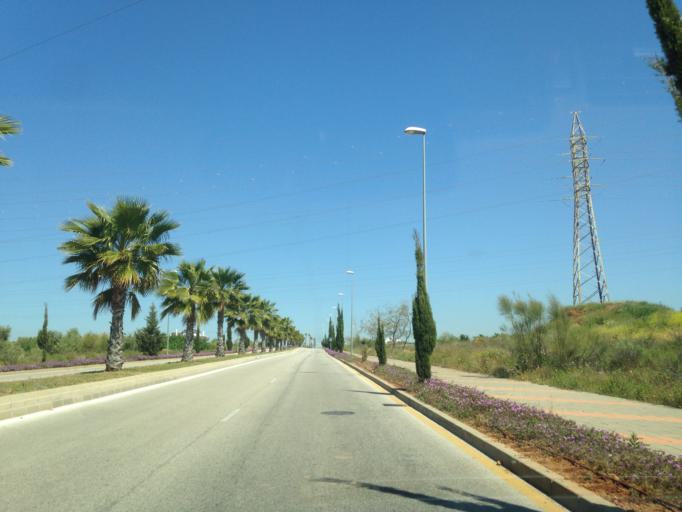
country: ES
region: Andalusia
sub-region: Provincia de Malaga
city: Malaga
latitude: 36.7298
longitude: -4.4888
